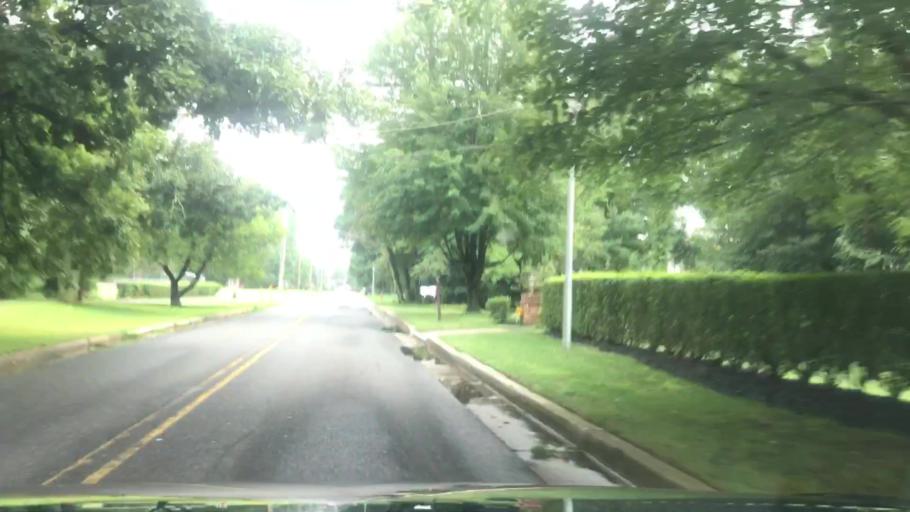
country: US
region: New Jersey
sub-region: Monmouth County
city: Fair Haven
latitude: 40.3480
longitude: -74.0405
